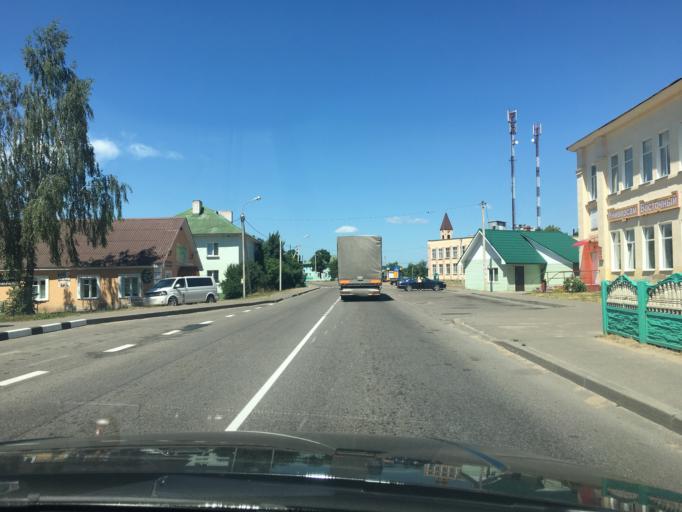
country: BY
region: Grodnenskaya
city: Iwye
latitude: 54.0315
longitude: 25.9272
